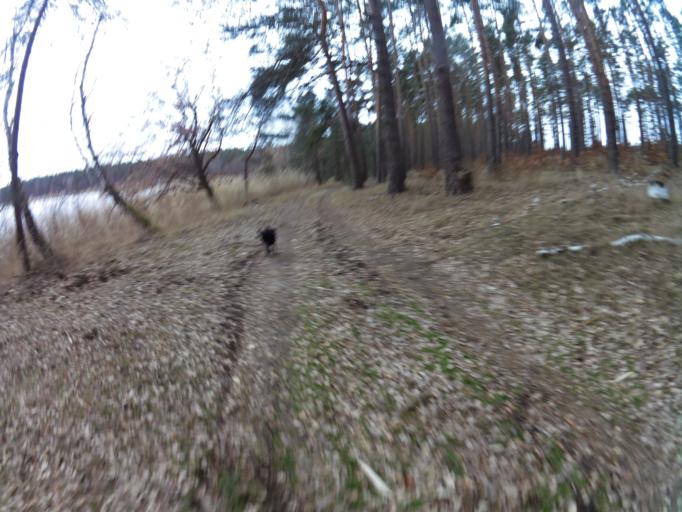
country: PL
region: West Pomeranian Voivodeship
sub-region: Powiat mysliborski
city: Debno
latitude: 52.7591
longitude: 14.7931
